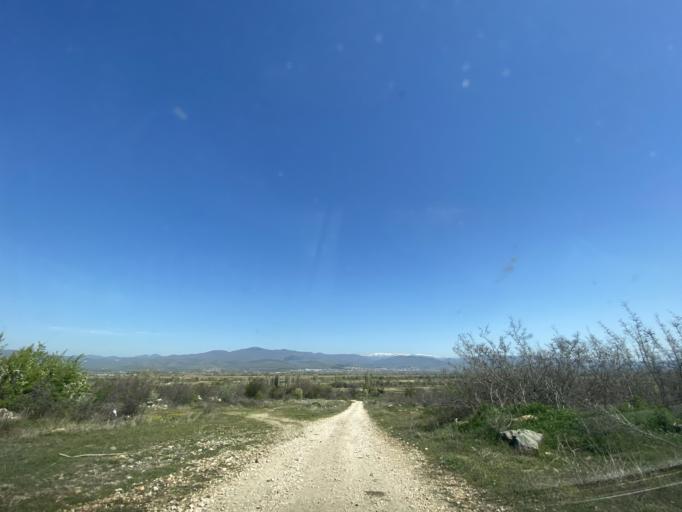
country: MK
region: Zrnovci
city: Zrnovci
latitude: 41.8518
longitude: 22.3894
